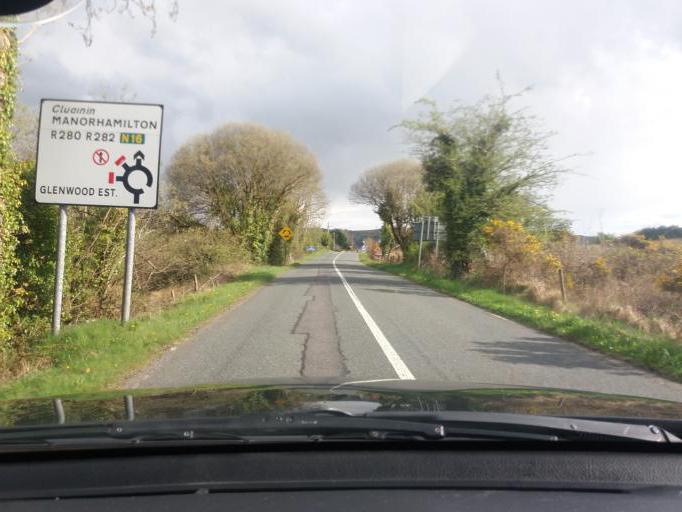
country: IE
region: Connaught
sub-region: County Leitrim
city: Manorhamilton
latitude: 54.3104
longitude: -8.1854
